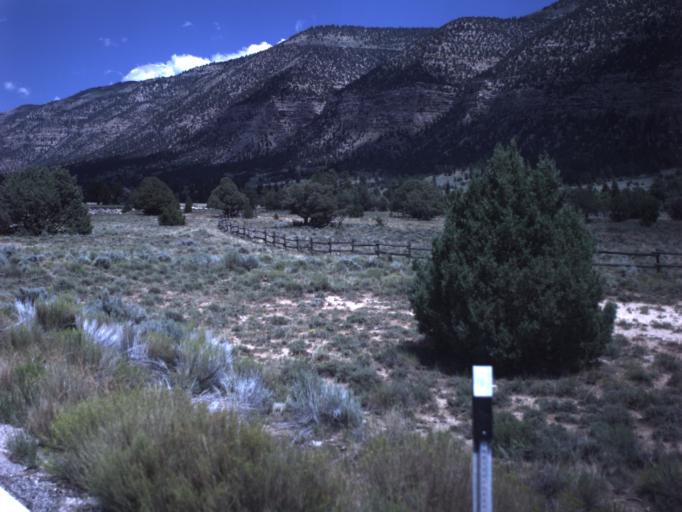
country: US
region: Utah
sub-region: Emery County
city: Orangeville
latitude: 39.3214
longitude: -111.2821
